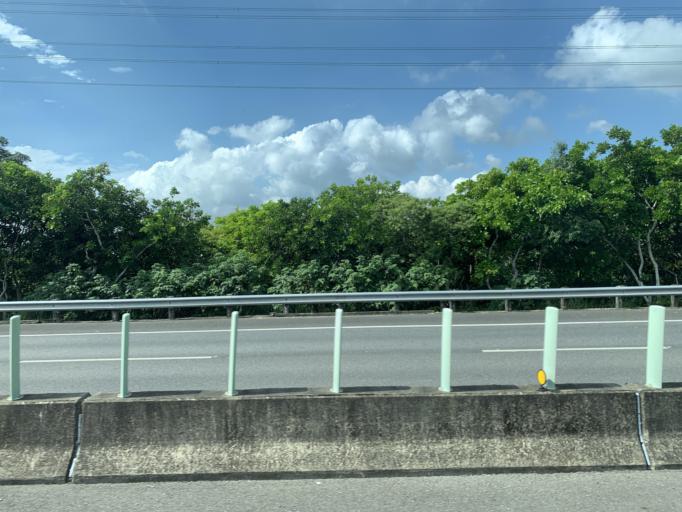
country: TW
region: Taiwan
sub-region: Pingtung
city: Pingtung
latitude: 22.8590
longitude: 120.4928
